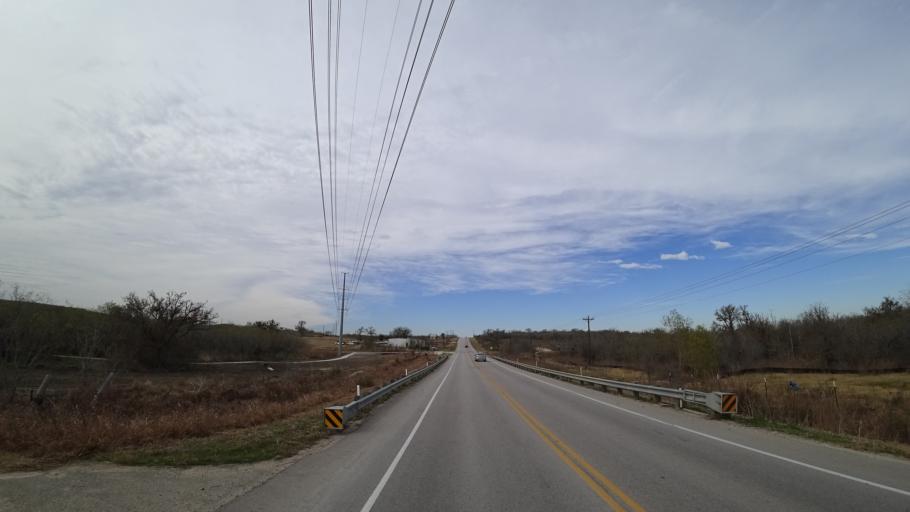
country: US
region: Texas
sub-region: Travis County
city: Garfield
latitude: 30.1541
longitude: -97.5915
